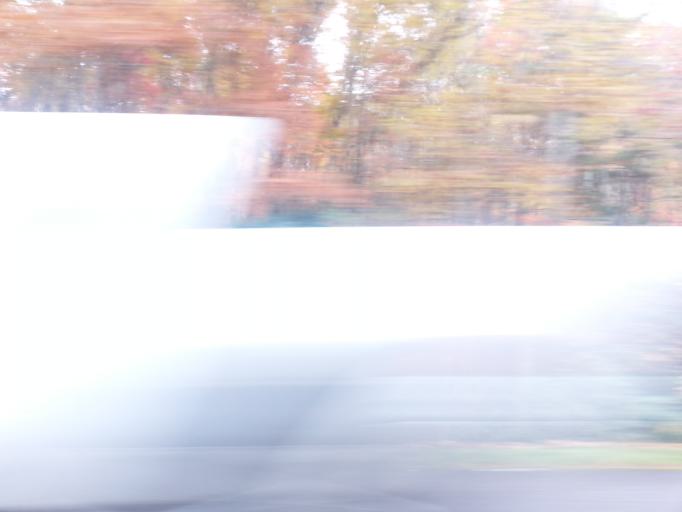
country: US
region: North Carolina
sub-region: Ashe County
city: Jefferson
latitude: 36.3115
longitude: -81.3618
